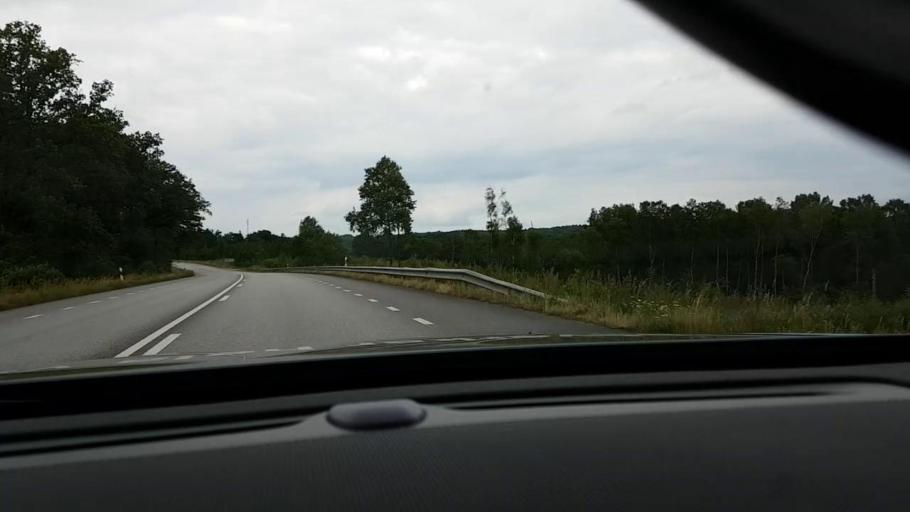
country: SE
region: Skane
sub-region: Hassleholms Kommun
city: Tormestorp
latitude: 56.0592
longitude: 13.7321
